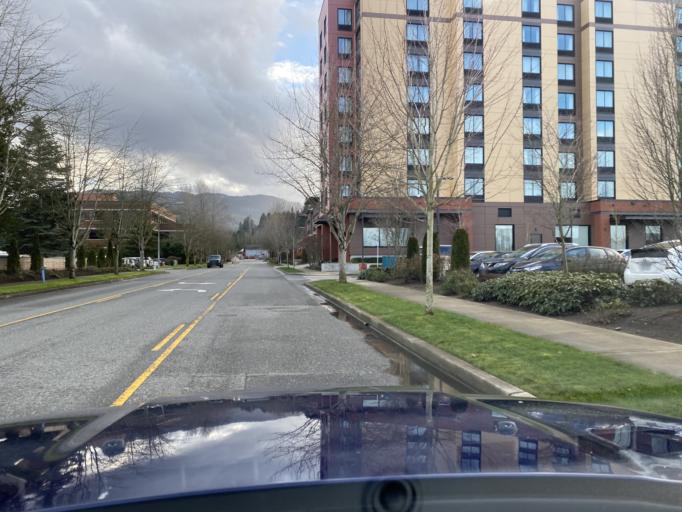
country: US
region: Washington
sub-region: King County
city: Issaquah
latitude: 47.5474
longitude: -122.0644
